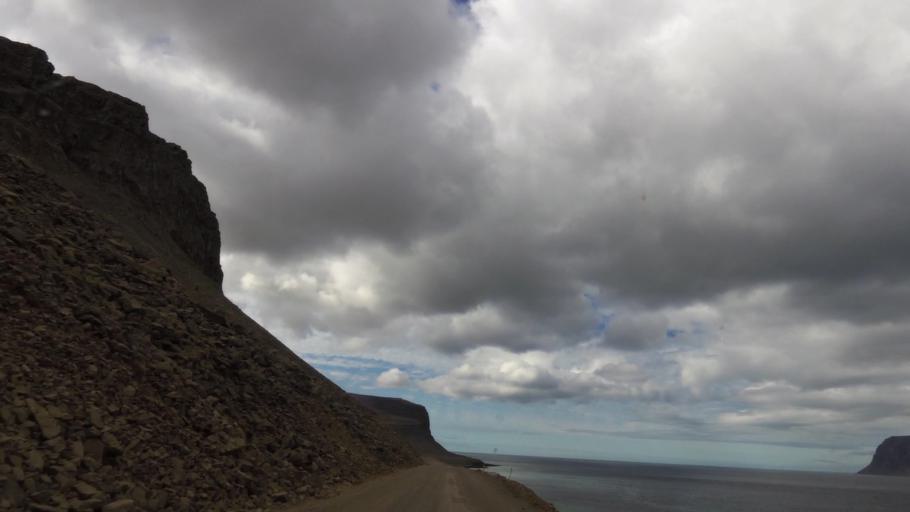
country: IS
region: West
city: Olafsvik
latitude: 65.5650
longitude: -24.0403
